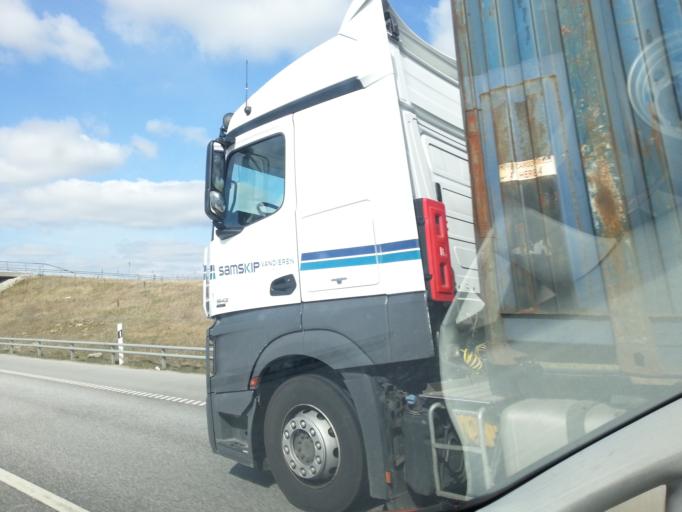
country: SE
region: Skane
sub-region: Vellinge Kommun
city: Vellinge
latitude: 55.4537
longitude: 13.0203
